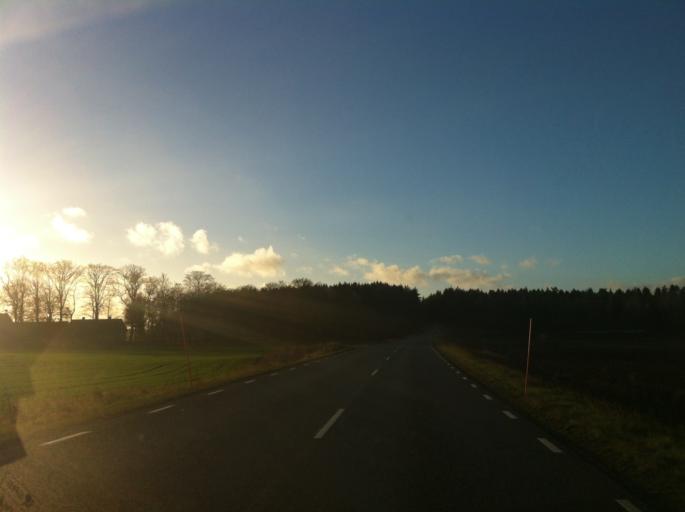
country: SE
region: Skane
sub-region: Ostra Goinge Kommun
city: Knislinge
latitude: 56.1887
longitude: 14.0446
